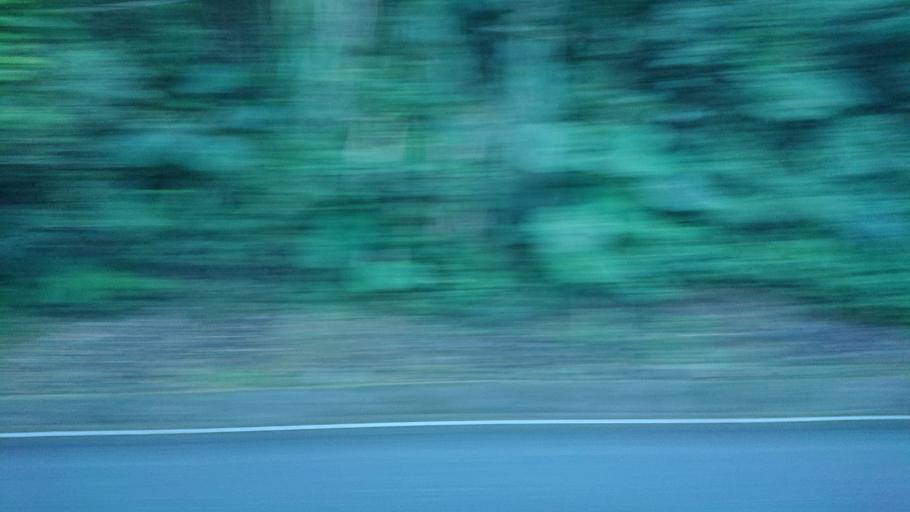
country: TW
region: Taiwan
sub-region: Chiayi
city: Jiayi Shi
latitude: 23.4707
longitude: 120.7186
